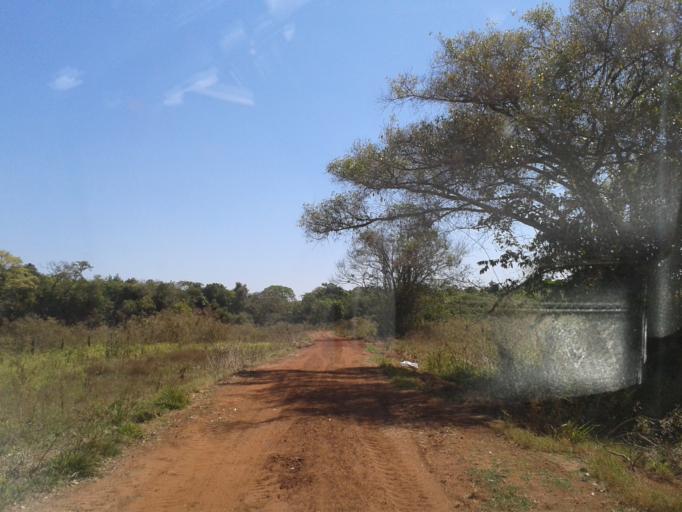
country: BR
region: Minas Gerais
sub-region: Santa Vitoria
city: Santa Vitoria
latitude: -19.0783
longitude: -50.0265
